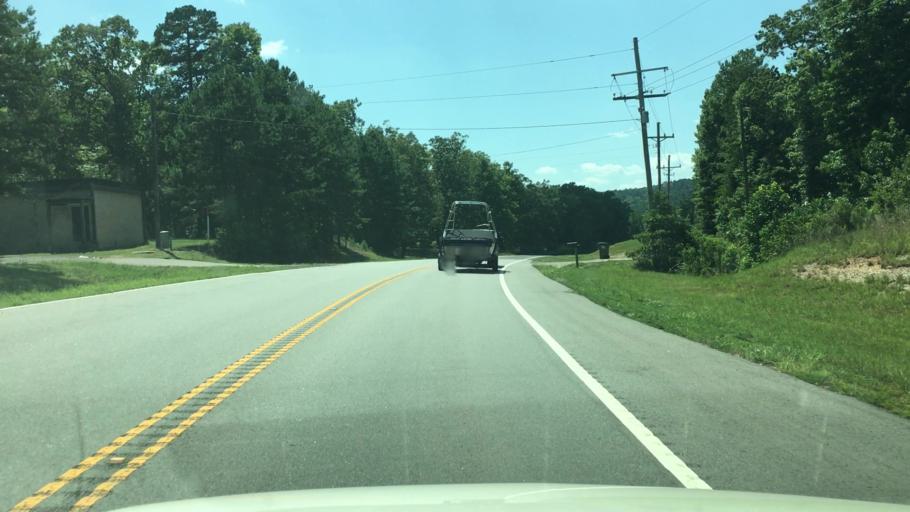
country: US
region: Arkansas
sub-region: Garland County
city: Rockwell
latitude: 34.5225
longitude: -93.3256
